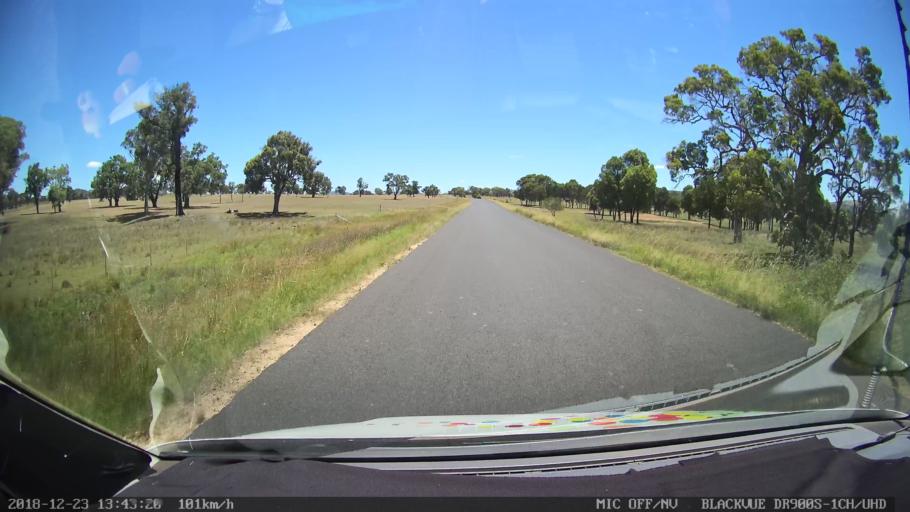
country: AU
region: New South Wales
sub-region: Tamworth Municipality
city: Manilla
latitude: -30.4853
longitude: 151.1518
